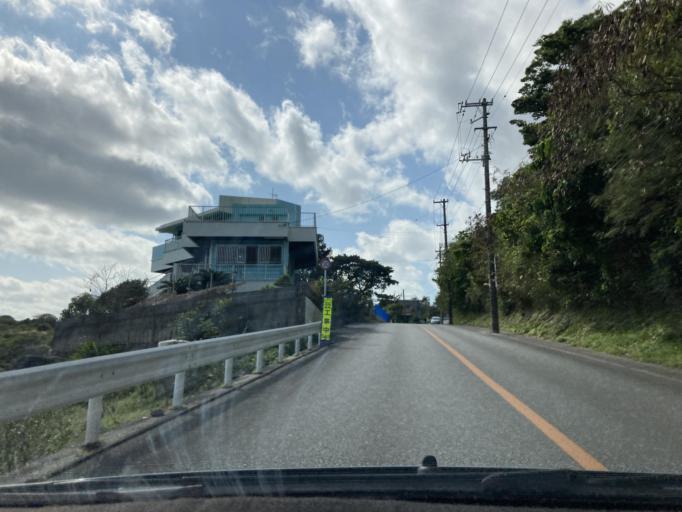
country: JP
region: Okinawa
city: Ginowan
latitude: 26.1837
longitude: 127.7614
